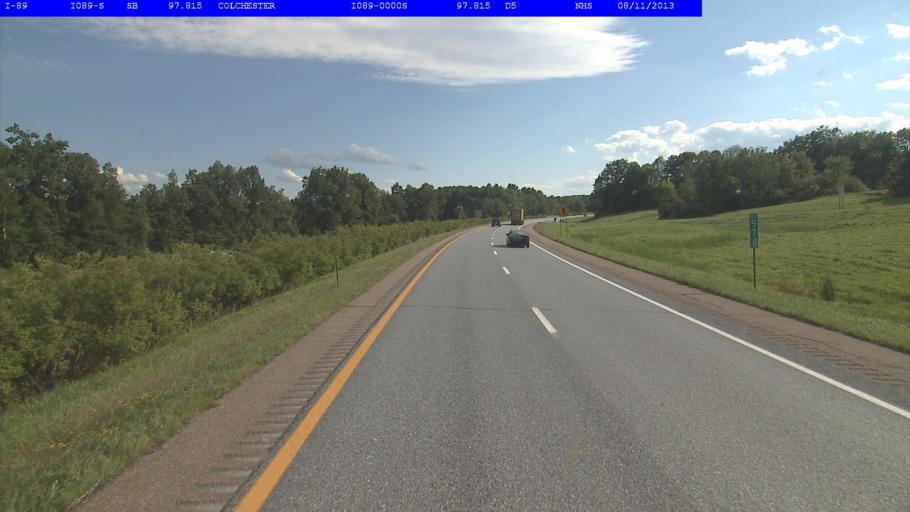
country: US
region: Vermont
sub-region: Chittenden County
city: Colchester
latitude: 44.5890
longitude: -73.1706
